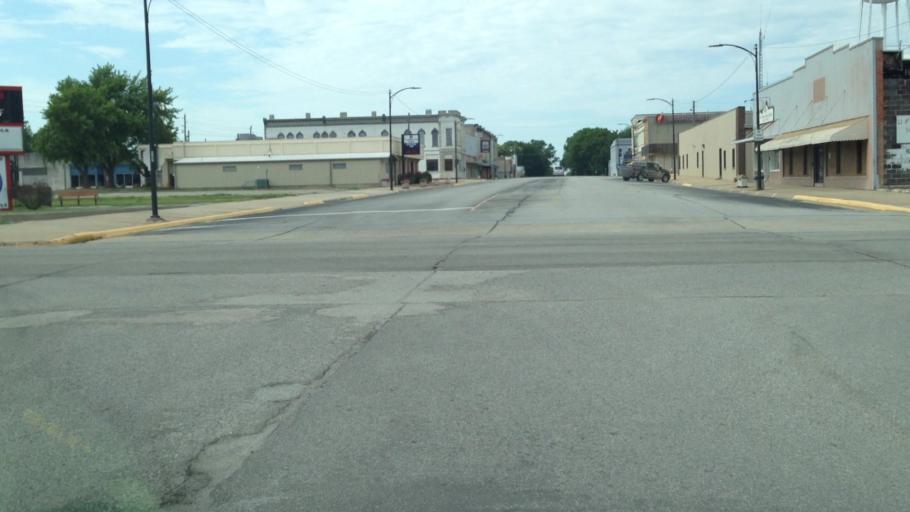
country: US
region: Kansas
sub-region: Labette County
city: Oswego
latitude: 37.1648
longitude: -95.1088
